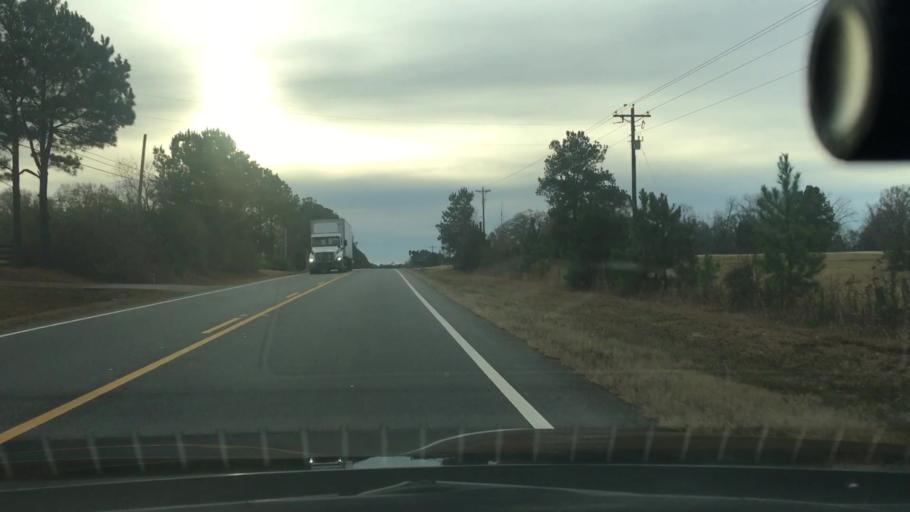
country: US
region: Georgia
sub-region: Coweta County
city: Senoia
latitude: 33.2694
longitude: -84.5254
